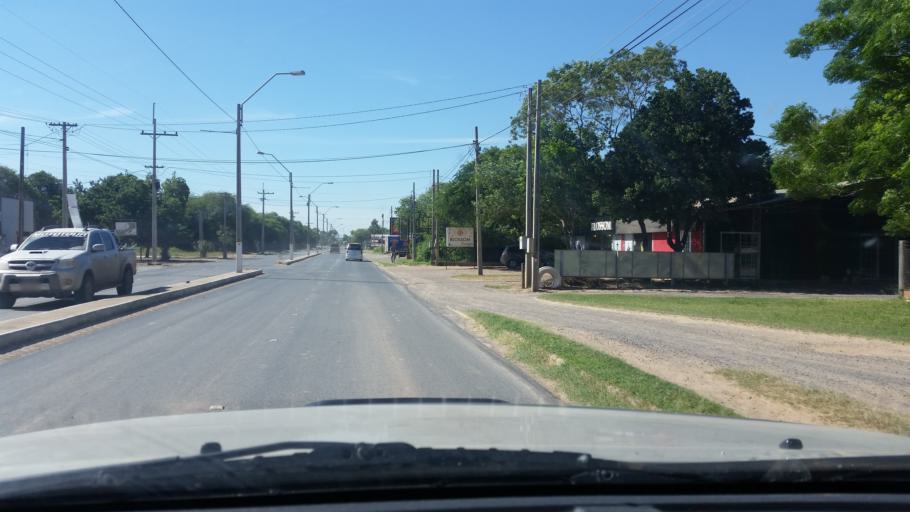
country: PY
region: Boqueron
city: Colonia Menno
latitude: -22.3731
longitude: -59.8373
